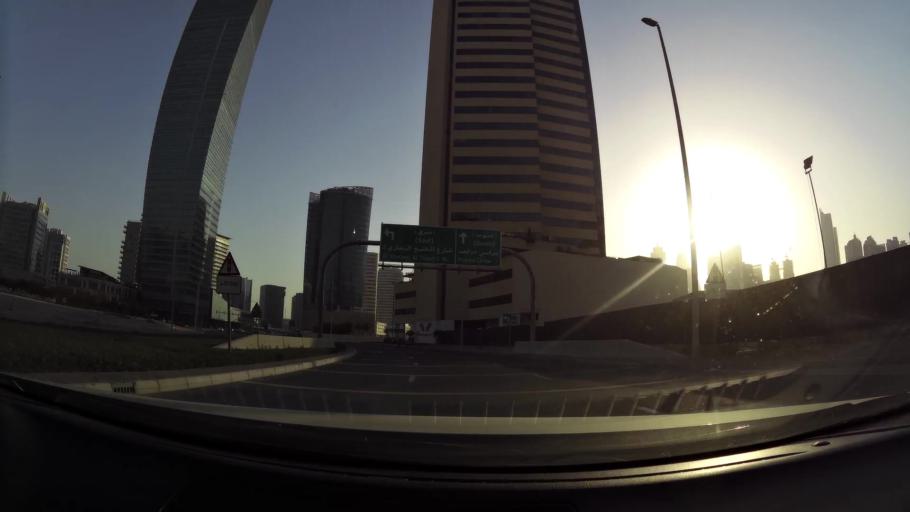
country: AE
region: Dubai
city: Dubai
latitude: 25.1825
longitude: 55.2729
